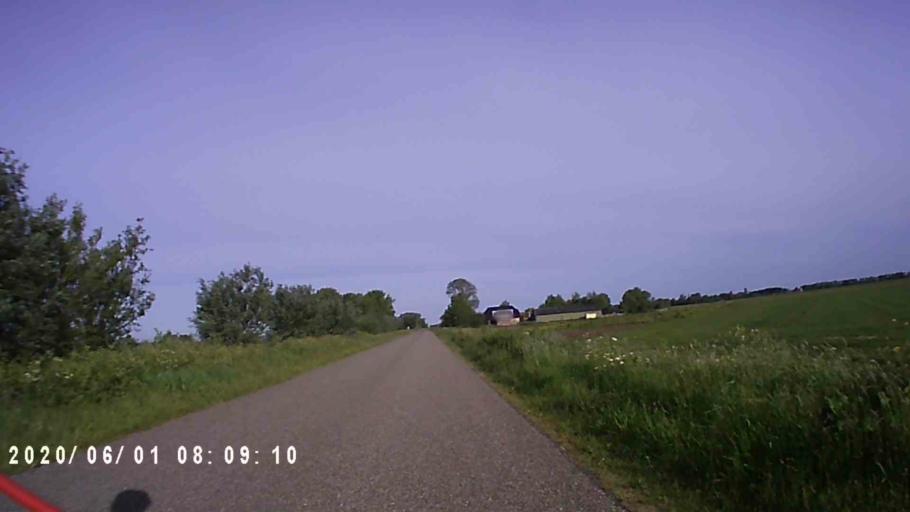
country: NL
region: Friesland
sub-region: Gemeente Ferwerderadiel
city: Burdaard
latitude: 53.2847
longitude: 5.8952
